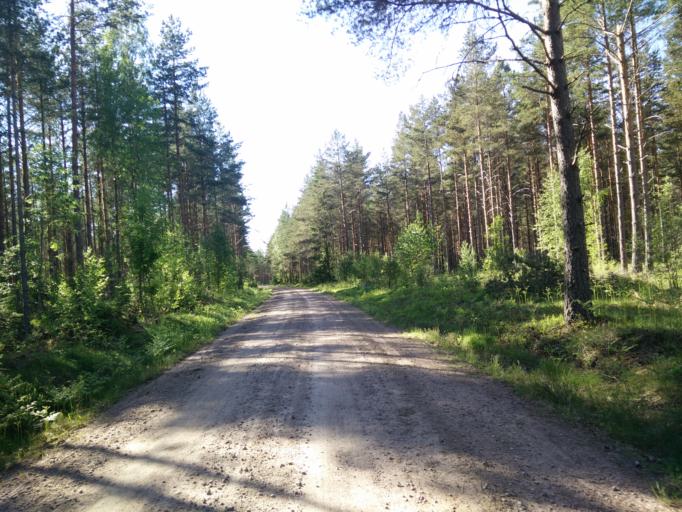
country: SE
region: Vaermland
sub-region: Hagfors Kommun
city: Hagfors
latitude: 60.0129
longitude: 13.5757
